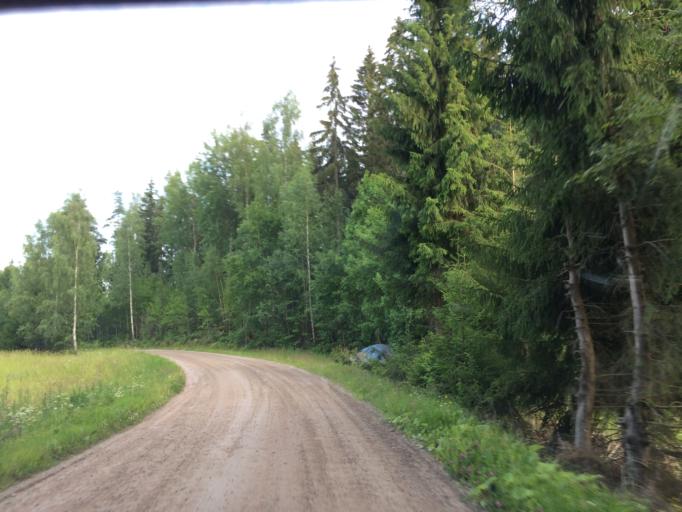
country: FI
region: Haeme
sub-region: Haemeenlinna
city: Janakkala
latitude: 60.8822
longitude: 24.6116
